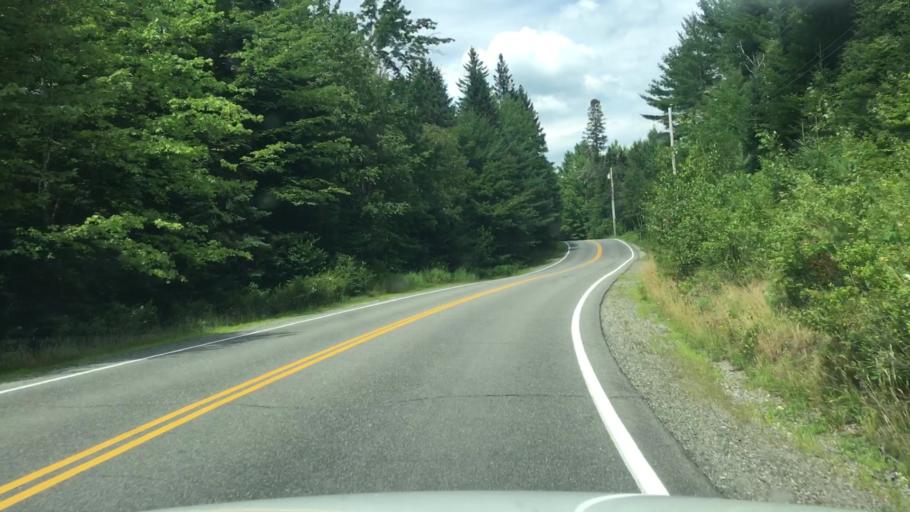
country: US
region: New Hampshire
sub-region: Grafton County
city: Deerfield
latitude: 44.2979
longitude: -71.6596
